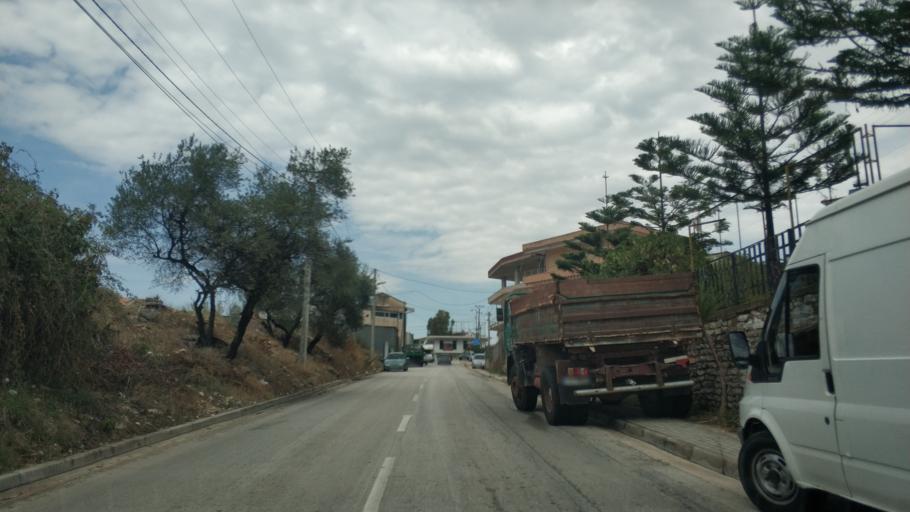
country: AL
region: Vlore
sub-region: Rrethi i Sarandes
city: Sarande
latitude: 39.8741
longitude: 20.0298
